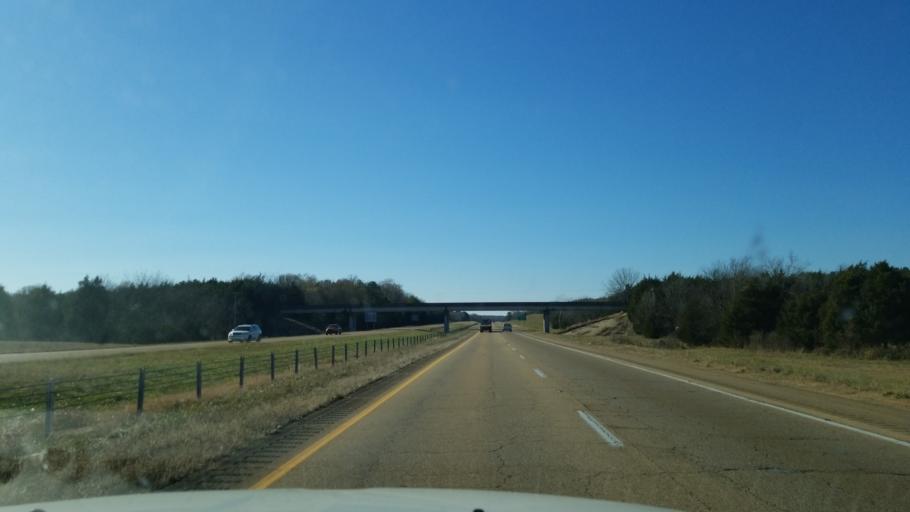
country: US
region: Mississippi
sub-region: Clay County
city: West Point
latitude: 33.4847
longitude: -88.6779
